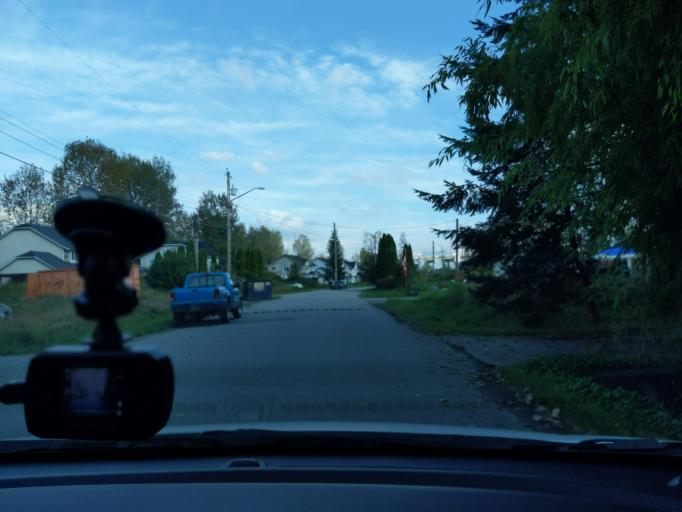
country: CA
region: British Columbia
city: Pitt Meadows
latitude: 49.2020
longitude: -122.6767
